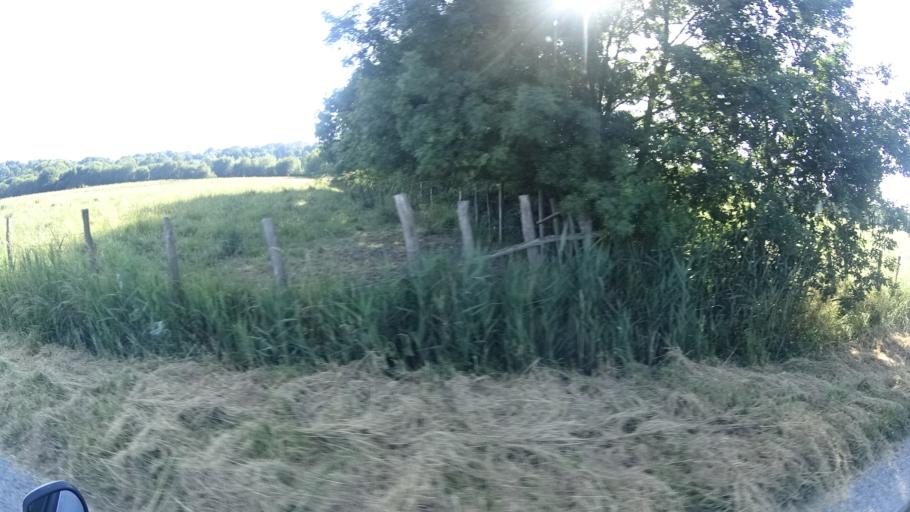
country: FR
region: Brittany
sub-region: Departement du Morbihan
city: Saint-Jean-la-Poterie
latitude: 47.6485
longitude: -2.1145
